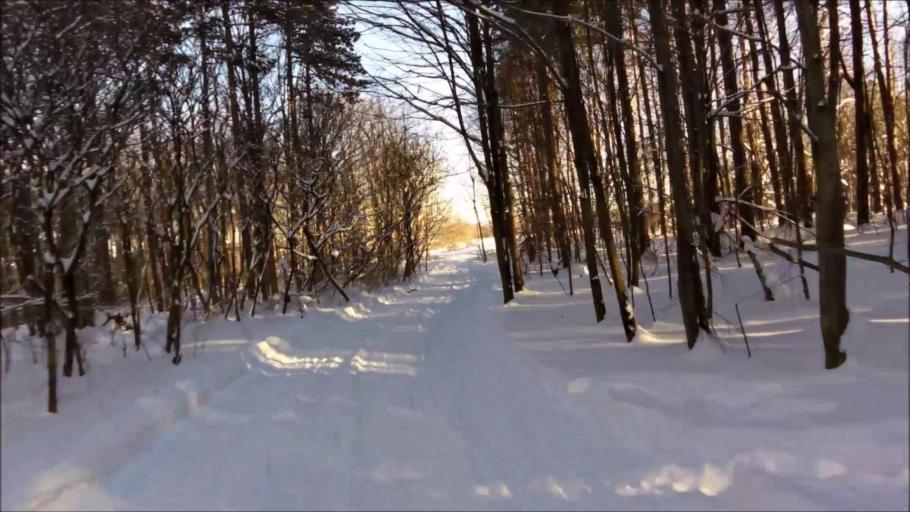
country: US
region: New York
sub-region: Chautauqua County
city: Mayville
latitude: 42.2671
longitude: -79.3806
